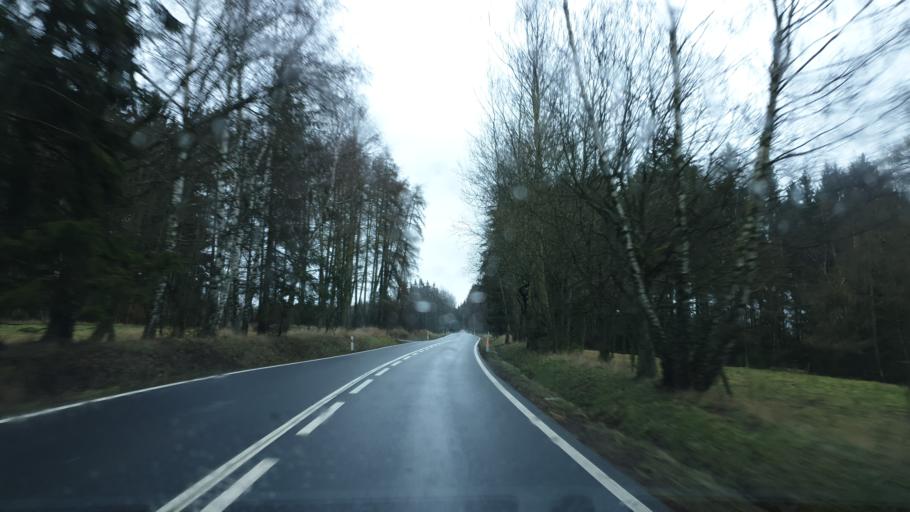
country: CZ
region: Karlovarsky
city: As
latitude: 50.2588
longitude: 12.1803
